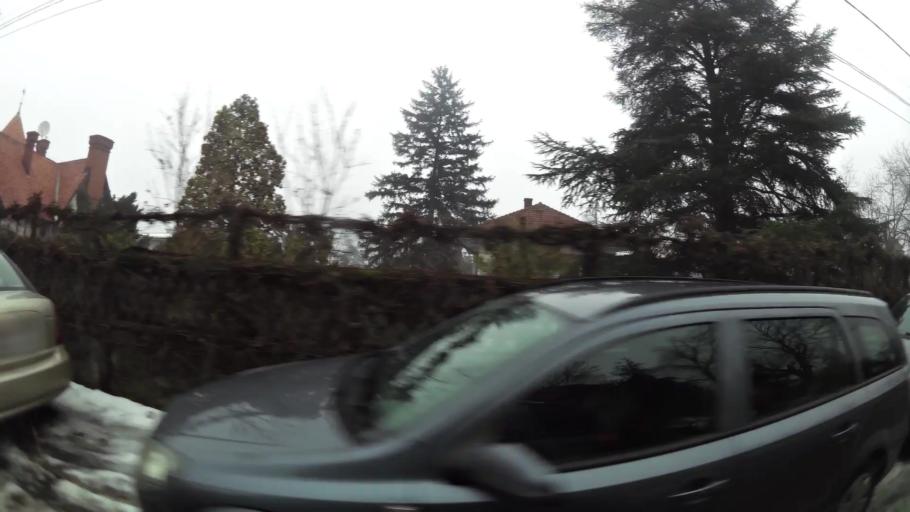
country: RS
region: Central Serbia
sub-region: Belgrade
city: Novi Beograd
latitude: 44.7919
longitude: 20.4380
